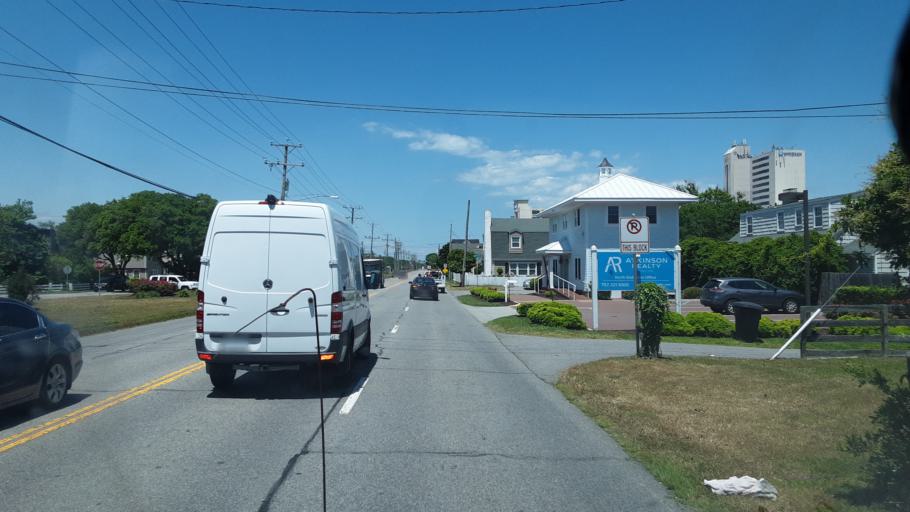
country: US
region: Virginia
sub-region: City of Virginia Beach
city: Virginia Beach
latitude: 36.8802
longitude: -75.9852
